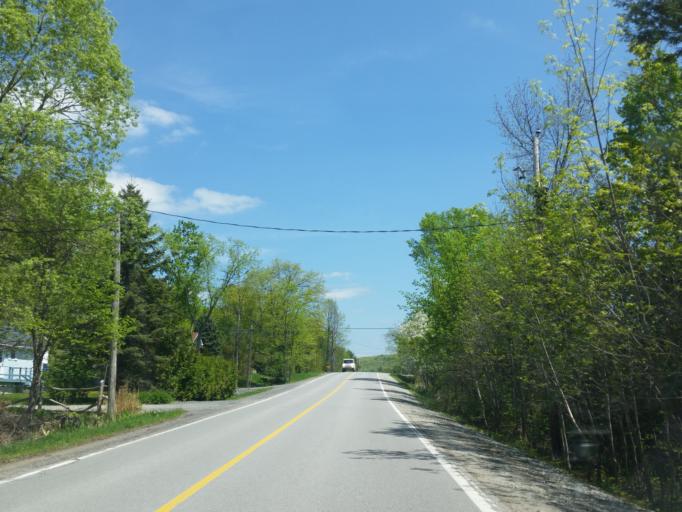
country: CA
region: Quebec
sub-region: Outaouais
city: Wakefield
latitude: 45.5823
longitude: -75.8749
